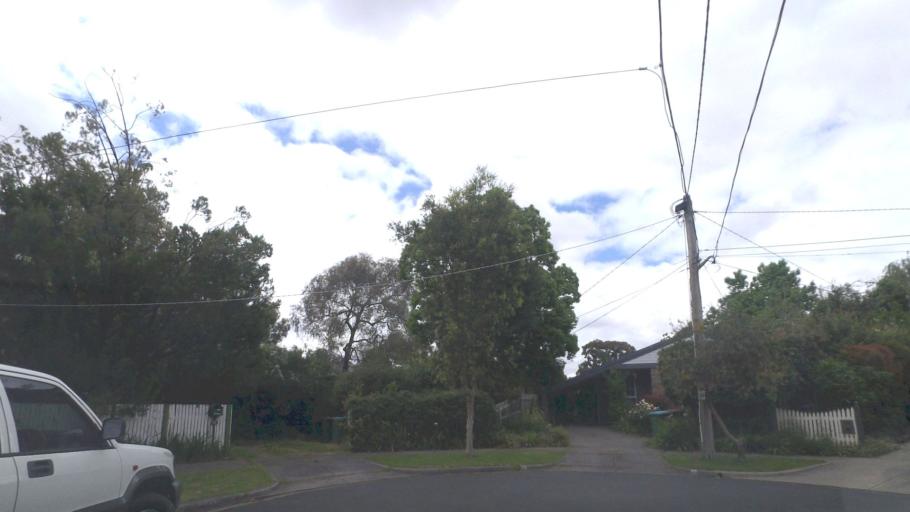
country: AU
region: Victoria
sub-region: Maroondah
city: Croydon North
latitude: -37.7905
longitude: 145.2867
